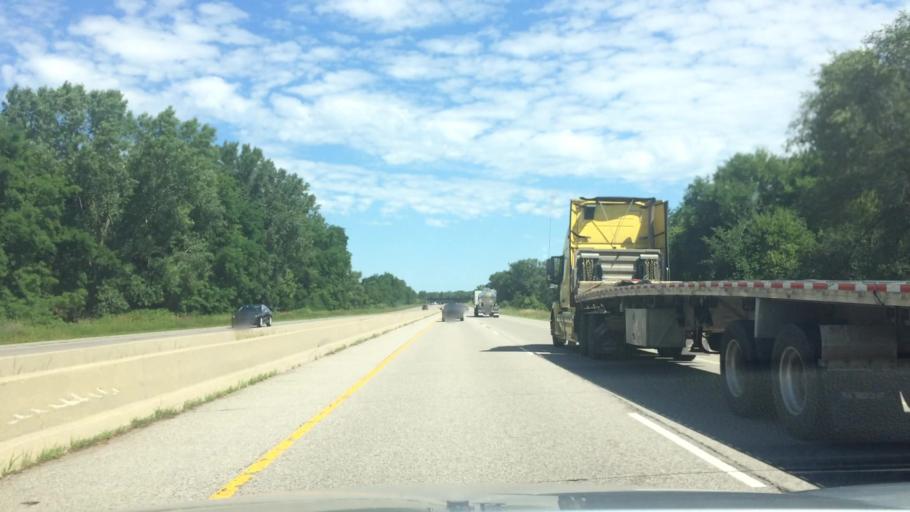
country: US
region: Wisconsin
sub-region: Marquette County
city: Westfield
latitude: 43.7423
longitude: -89.4825
